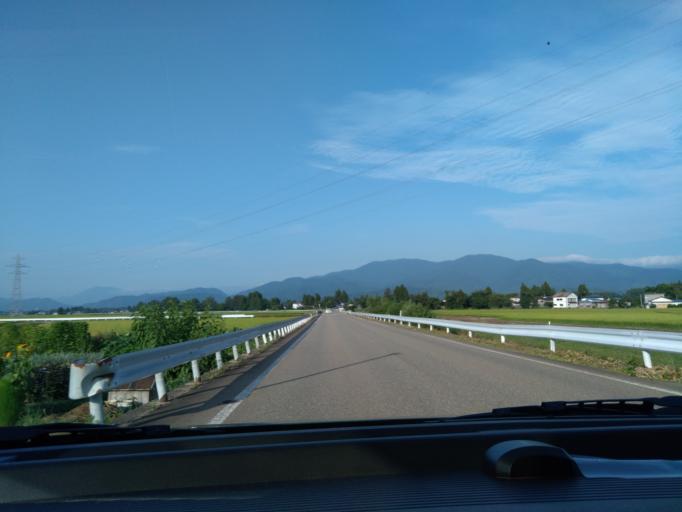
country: JP
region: Akita
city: Kakunodatemachi
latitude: 39.5563
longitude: 140.5682
